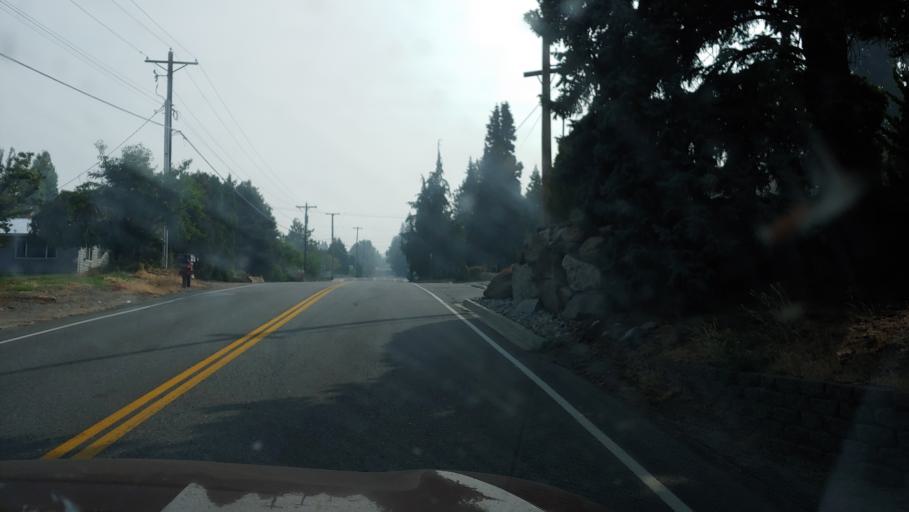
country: US
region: Washington
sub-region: Douglas County
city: East Wenatchee Bench
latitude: 47.4353
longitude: -120.2947
